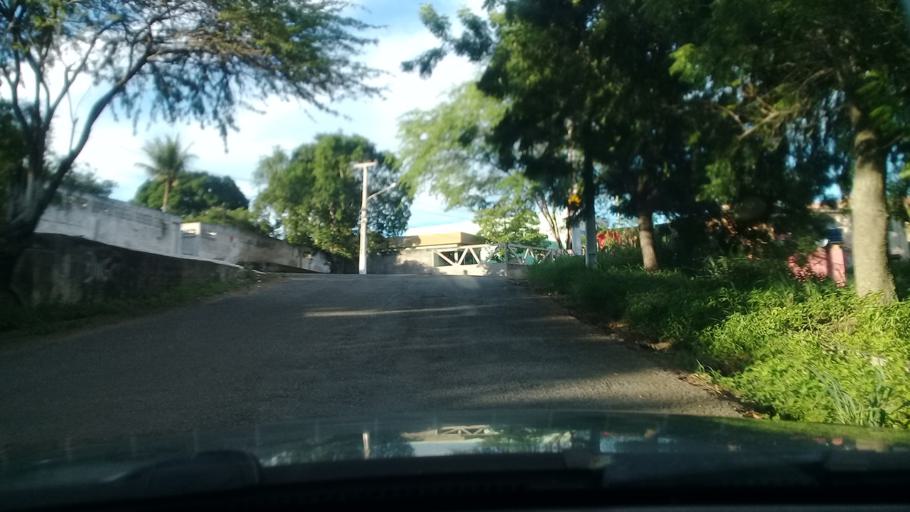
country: BR
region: Pernambuco
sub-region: Vicencia
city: Vicencia
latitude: -7.6094
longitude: -35.2346
